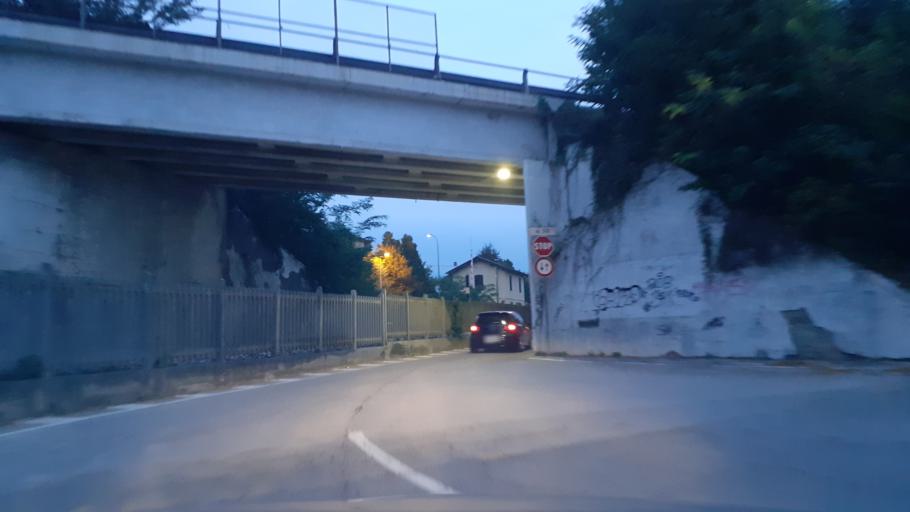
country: IT
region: Lombardy
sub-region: Provincia di Lecco
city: Bulciago
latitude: 45.7486
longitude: 9.2818
